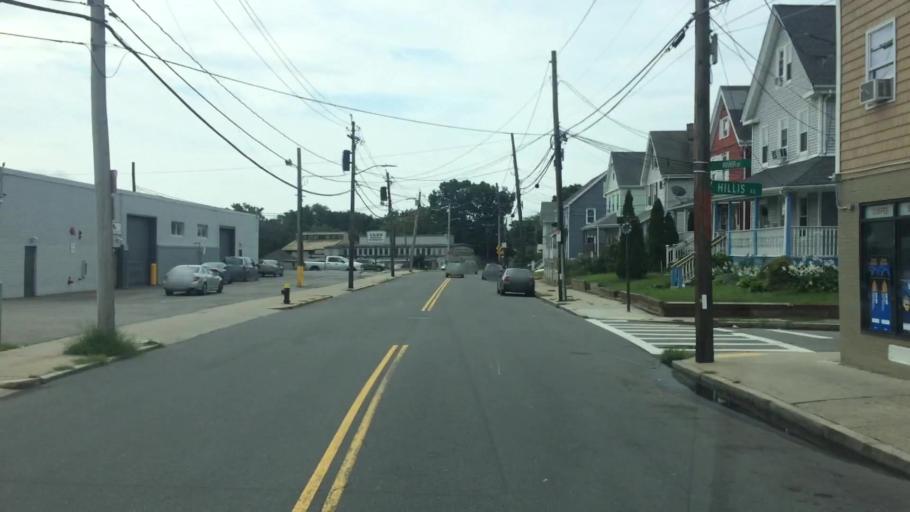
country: US
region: Massachusetts
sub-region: Norfolk County
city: Dedham
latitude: 42.2505
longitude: -71.1309
